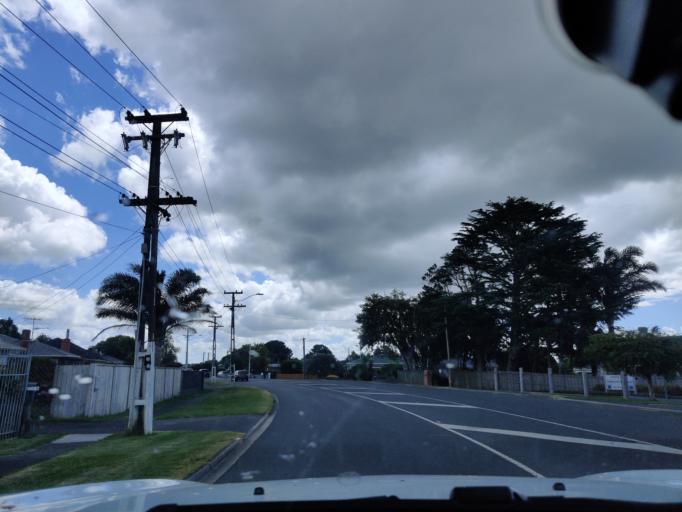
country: NZ
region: Auckland
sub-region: Auckland
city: Red Hill
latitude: -37.0539
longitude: 174.9608
